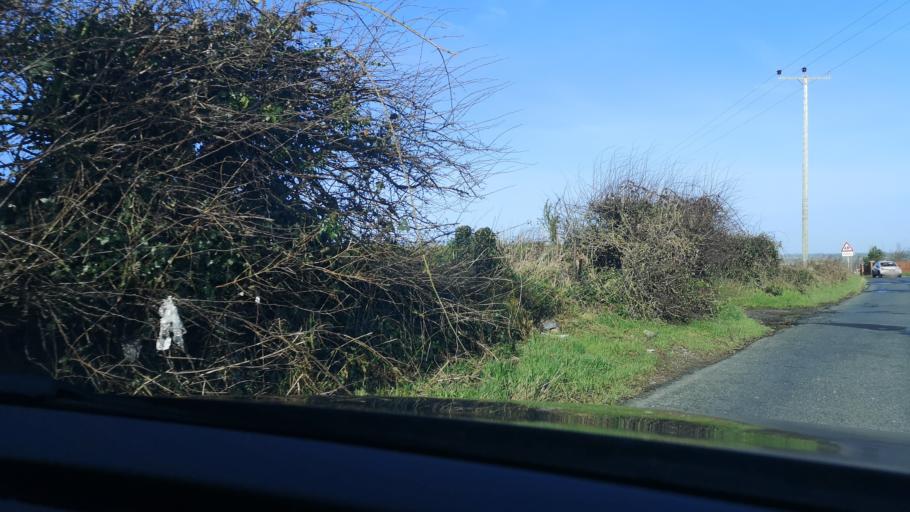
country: GB
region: Northern Ireland
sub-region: Newry and Mourne District
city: Newry
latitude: 54.1734
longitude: -6.3531
